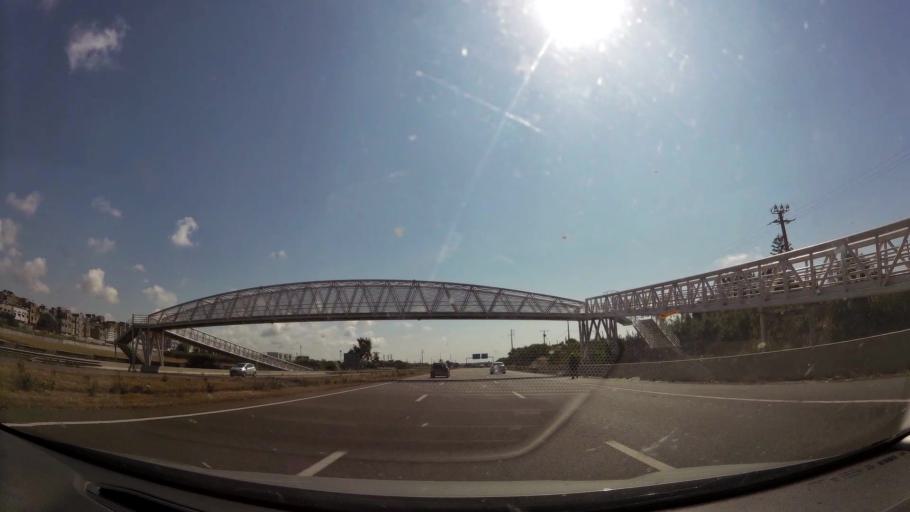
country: MA
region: Rabat-Sale-Zemmour-Zaer
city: Skhirat
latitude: 33.8589
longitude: -7.0348
